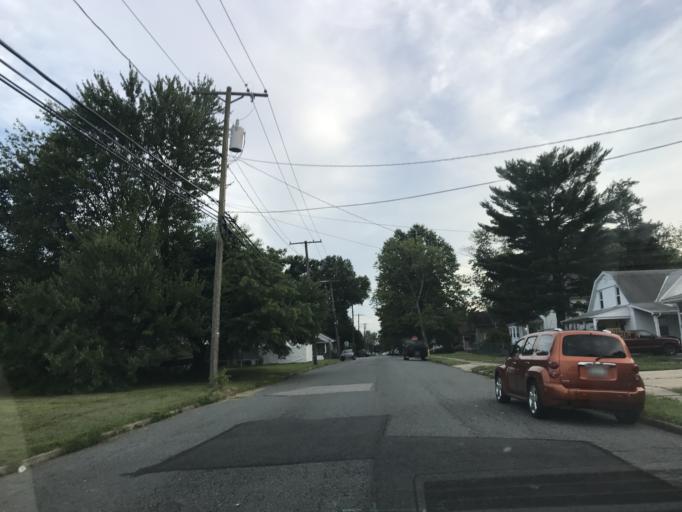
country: US
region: Maryland
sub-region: Harford County
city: Aberdeen
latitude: 39.5082
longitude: -76.1666
